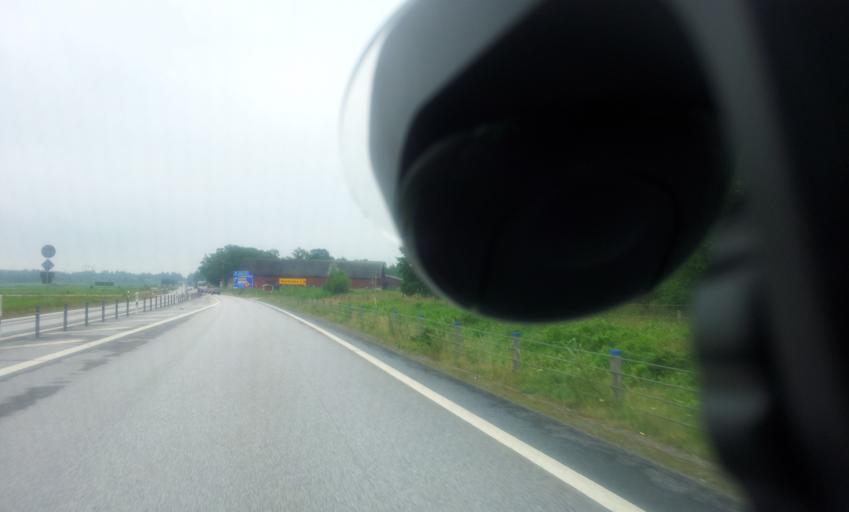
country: SE
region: Kalmar
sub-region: Vasterviks Kommun
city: Vaestervik
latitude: 57.7793
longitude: 16.5364
